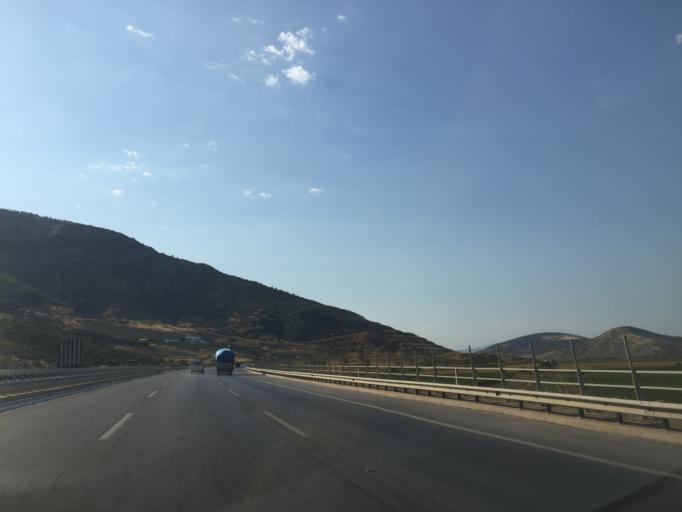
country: TR
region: Izmir
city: Belevi
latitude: 38.0297
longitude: 27.4338
